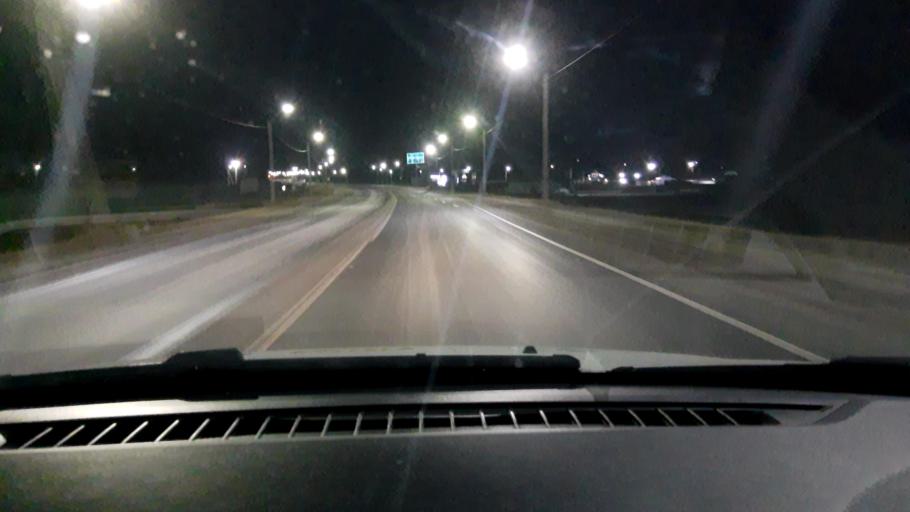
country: RU
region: Nizjnij Novgorod
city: Sitniki
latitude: 56.4987
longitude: 44.0253
